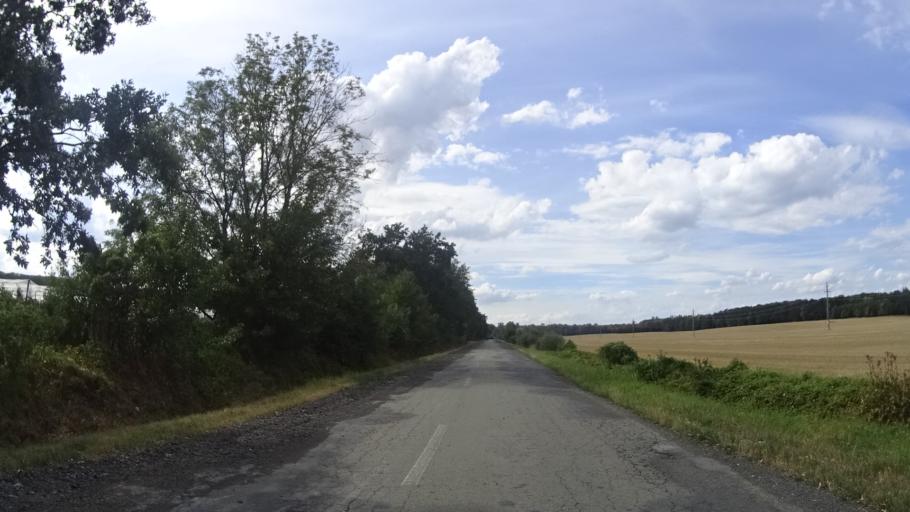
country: CZ
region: Olomoucky
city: Cervenka
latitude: 49.7168
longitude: 17.0456
